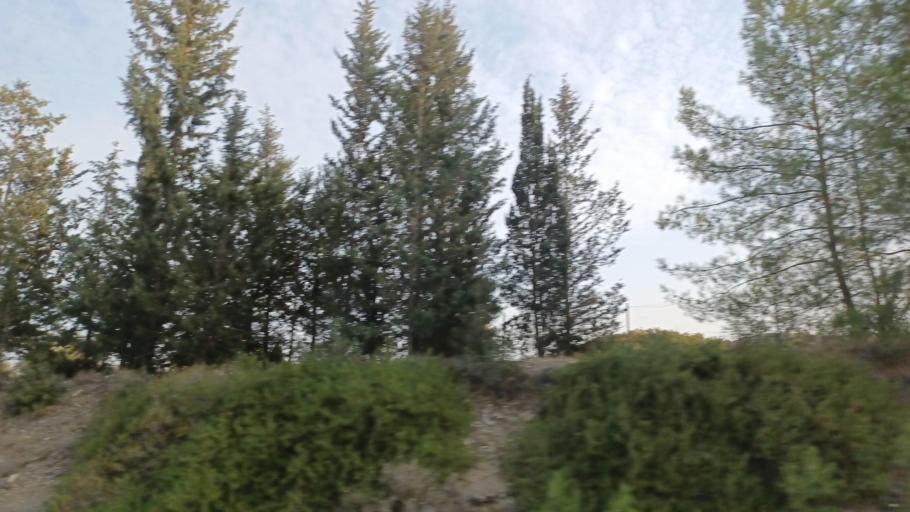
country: CY
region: Larnaka
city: Kofinou
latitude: 34.8336
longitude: 33.4100
